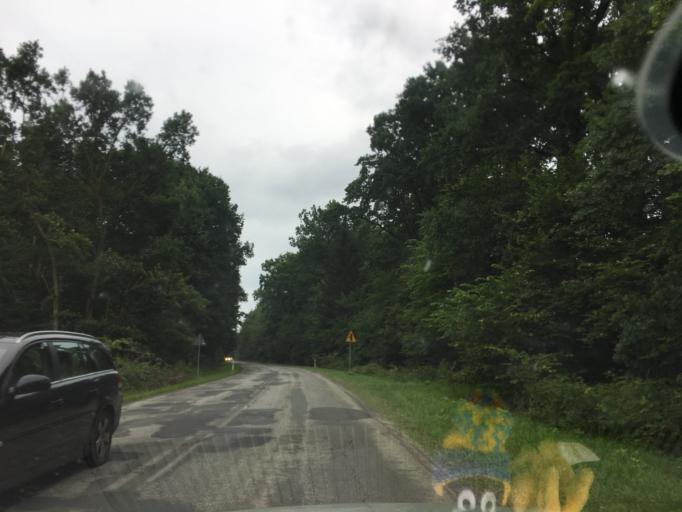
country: PL
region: West Pomeranian Voivodeship
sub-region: Powiat gryficki
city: Pobierowo
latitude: 54.0497
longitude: 14.9319
